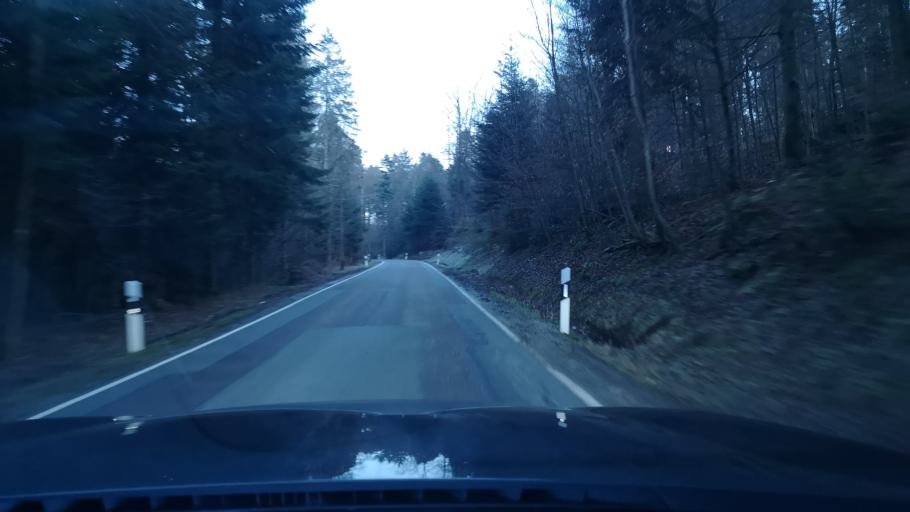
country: DE
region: Baden-Wuerttemberg
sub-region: Regierungsbezirk Stuttgart
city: Gschwend
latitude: 48.9320
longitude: 9.7075
